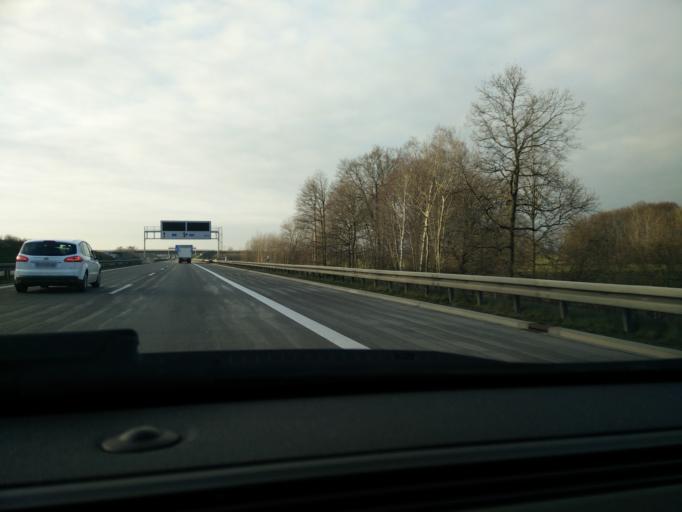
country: DE
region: Saxony
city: Naunhof
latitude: 51.3101
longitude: 12.5638
